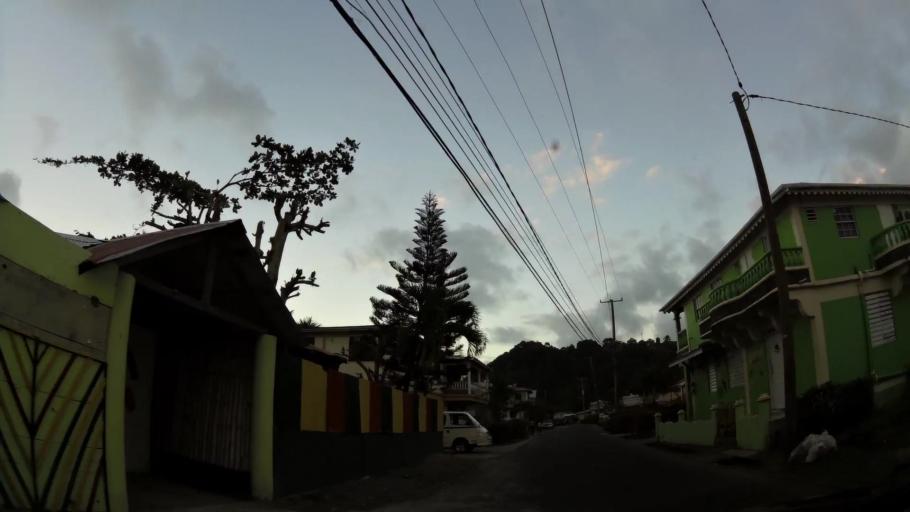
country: DM
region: Saint Andrew
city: Calibishie
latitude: 15.5931
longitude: -61.3509
